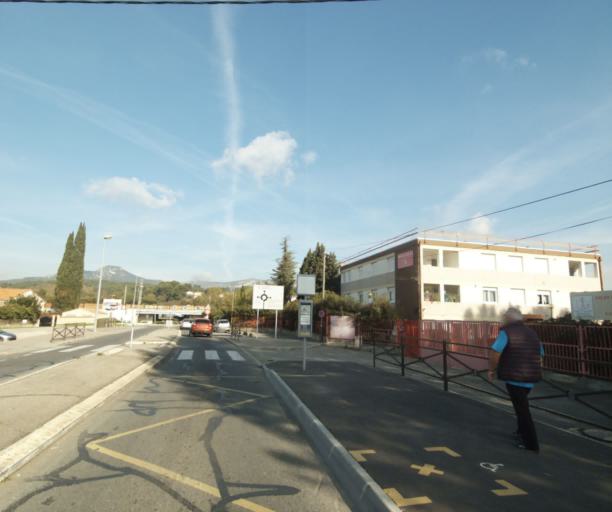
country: FR
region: Provence-Alpes-Cote d'Azur
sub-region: Departement des Bouches-du-Rhone
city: Aubagne
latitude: 43.2867
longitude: 5.5485
